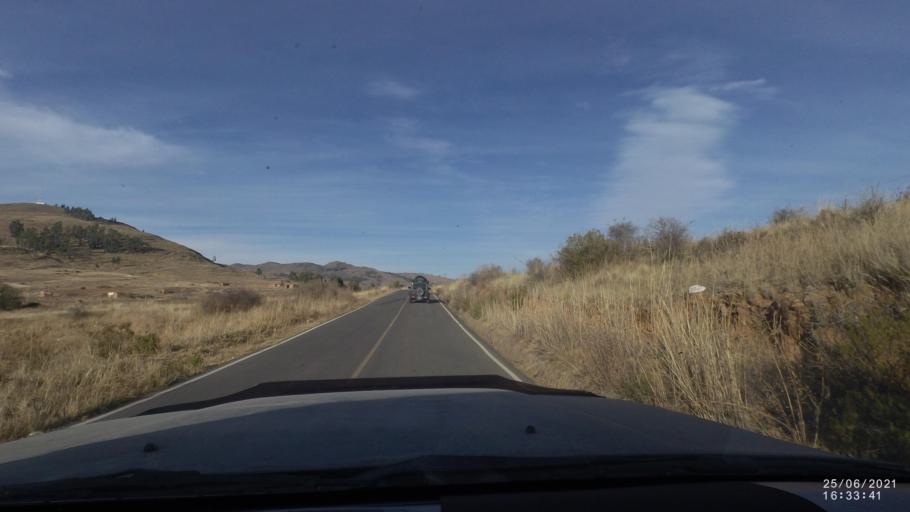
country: BO
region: Cochabamba
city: Arani
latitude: -17.8120
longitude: -65.7856
